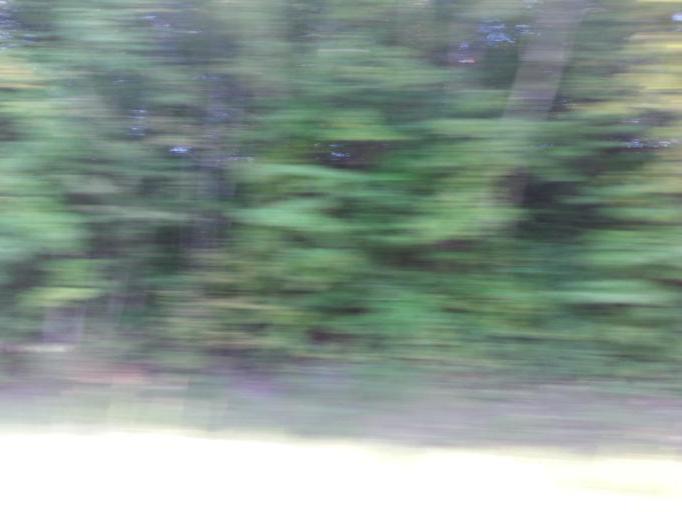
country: US
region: Alabama
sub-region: Lauderdale County
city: Killen
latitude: 34.8597
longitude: -87.5220
